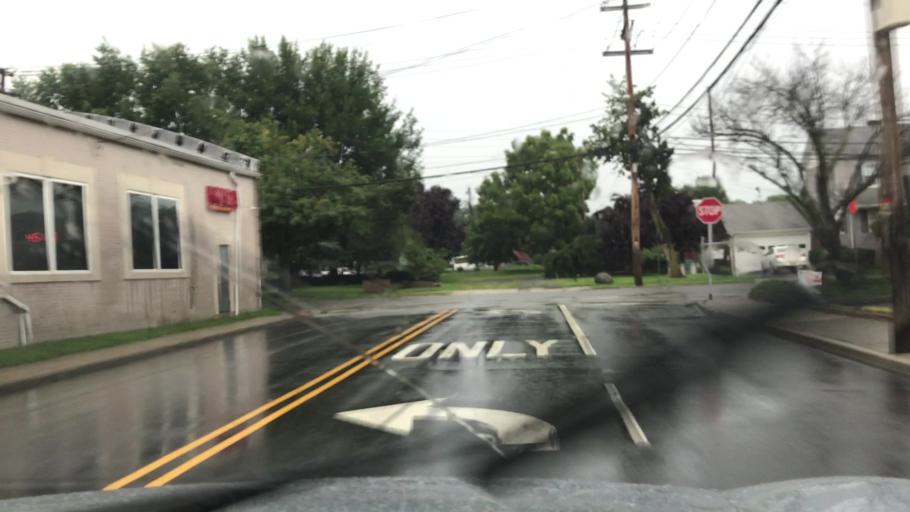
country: US
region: New Jersey
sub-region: Bergen County
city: Closter
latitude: 40.9735
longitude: -73.9601
